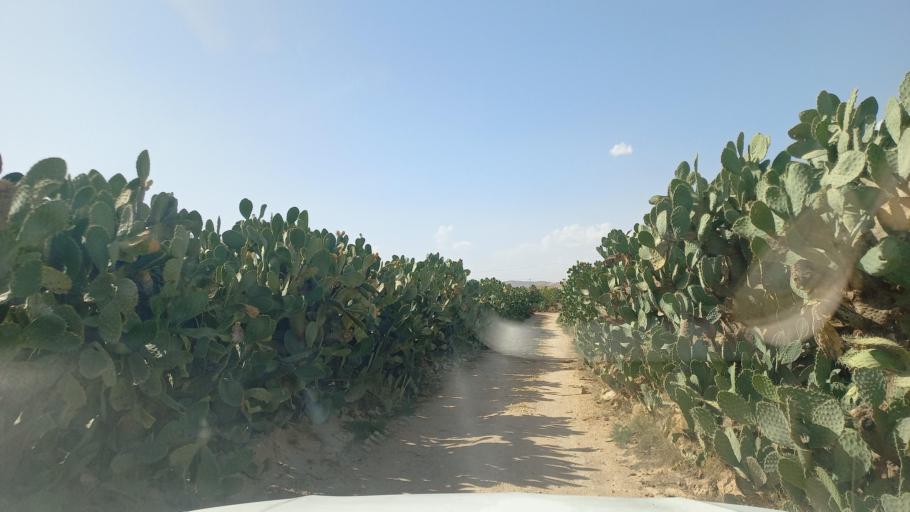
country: TN
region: Al Qasrayn
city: Sbiba
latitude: 35.3032
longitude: 9.0415
